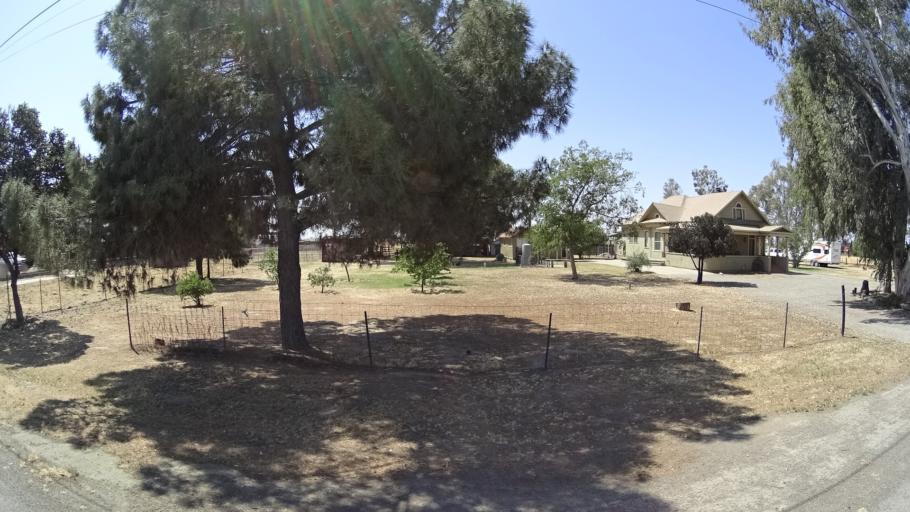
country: US
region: California
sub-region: Kings County
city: Home Garden
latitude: 36.2841
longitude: -119.6289
